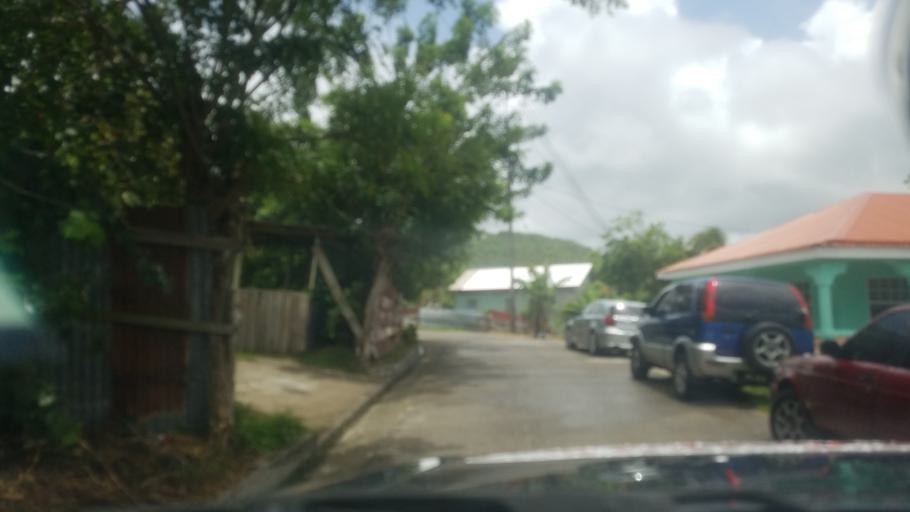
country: LC
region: Vieux-Fort
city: Vieux Fort
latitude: 13.7441
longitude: -60.9557
